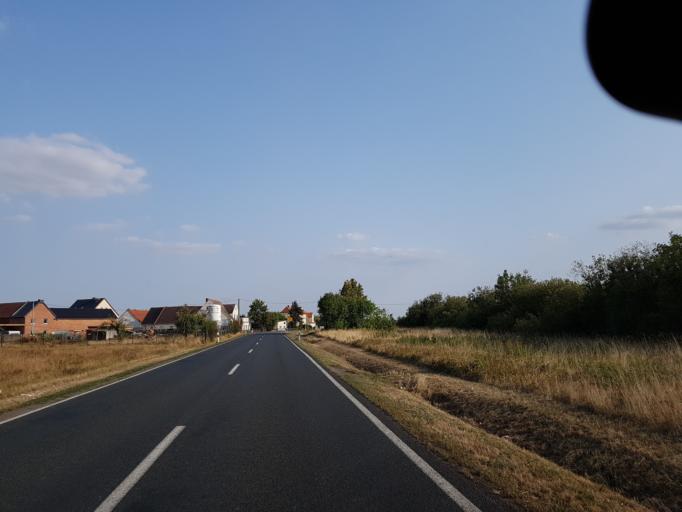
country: DE
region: Saxony
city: Elsnig
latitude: 51.5980
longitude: 12.9444
